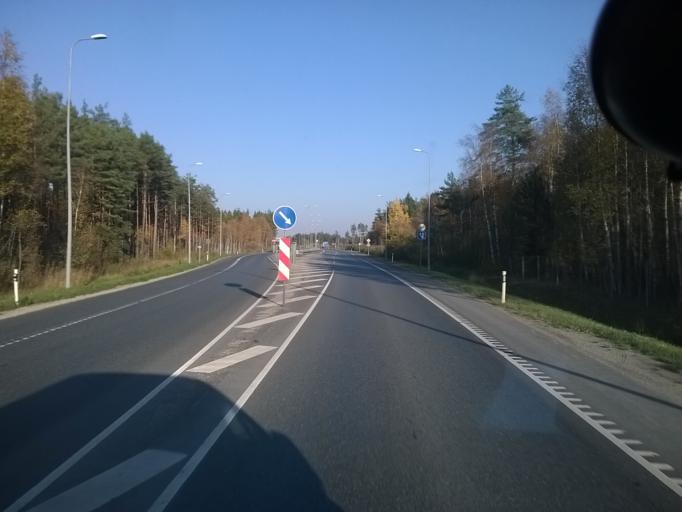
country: EE
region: Harju
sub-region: Saku vald
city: Saku
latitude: 59.3137
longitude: 24.7449
